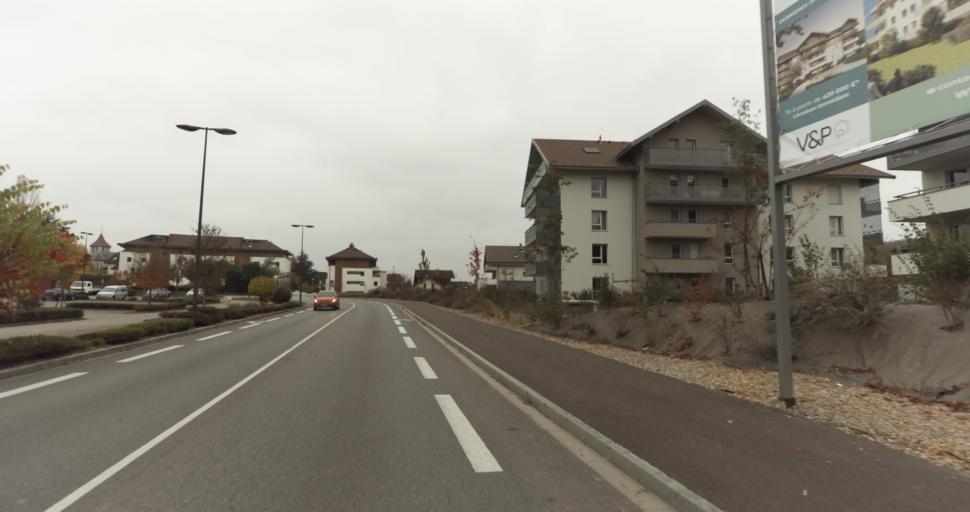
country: FR
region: Rhone-Alpes
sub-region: Departement de la Haute-Savoie
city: Poisy
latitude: 45.9250
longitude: 6.0614
